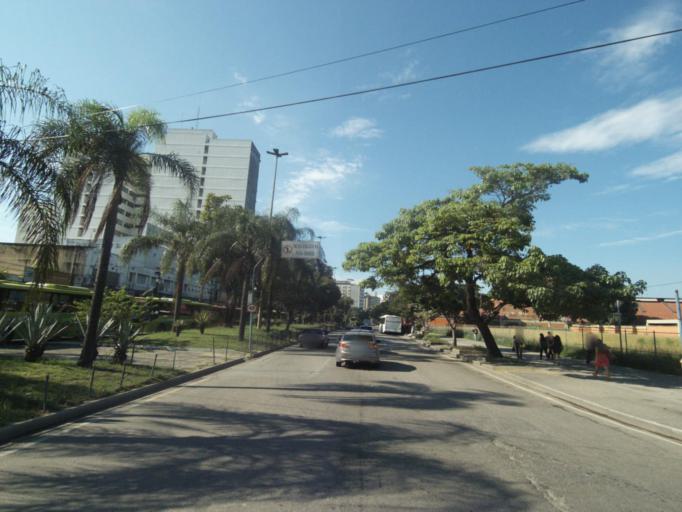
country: BR
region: Rio de Janeiro
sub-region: Niteroi
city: Niteroi
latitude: -22.8901
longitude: -43.1242
